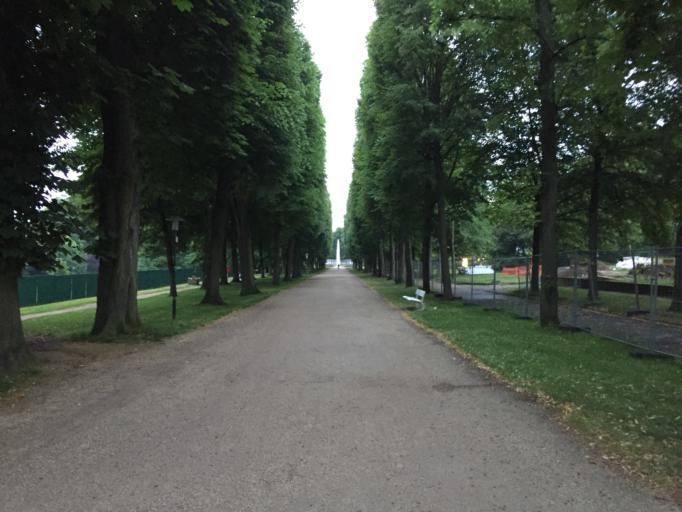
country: DE
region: Lower Saxony
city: Bad Pyrmont
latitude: 51.9870
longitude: 9.2508
